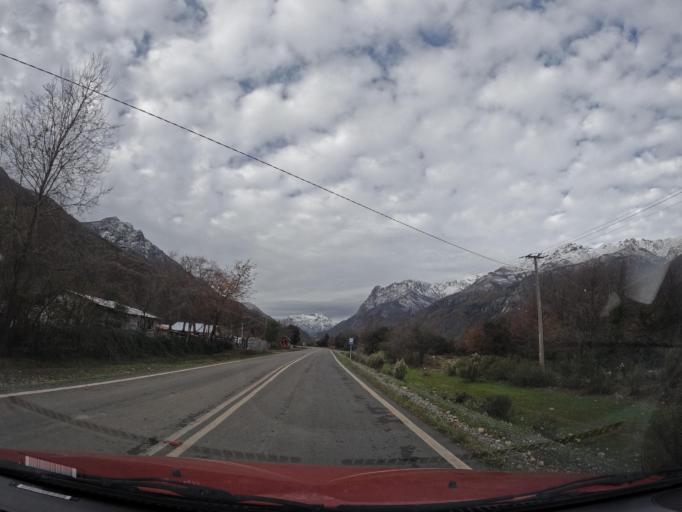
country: CL
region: Maule
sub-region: Provincia de Linares
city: Colbun
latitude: -35.8602
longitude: -71.2518
